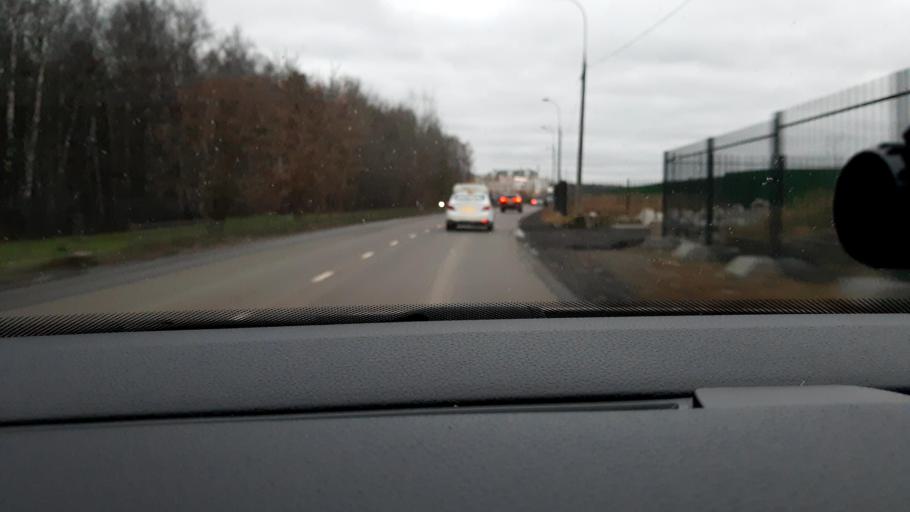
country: RU
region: Moskovskaya
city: Zarech'ye
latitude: 55.6812
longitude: 37.3989
